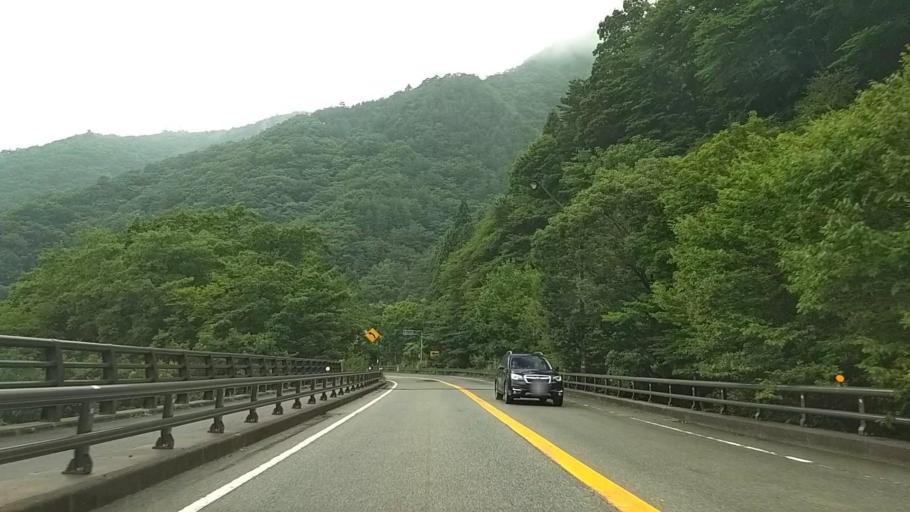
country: JP
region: Yamanashi
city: Fujikawaguchiko
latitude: 35.4890
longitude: 138.6254
